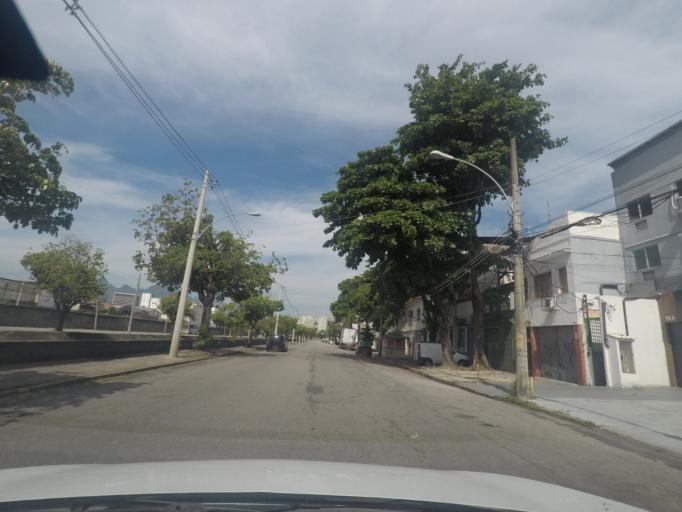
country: BR
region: Rio de Janeiro
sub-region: Rio De Janeiro
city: Rio de Janeiro
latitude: -22.9069
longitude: -43.2144
